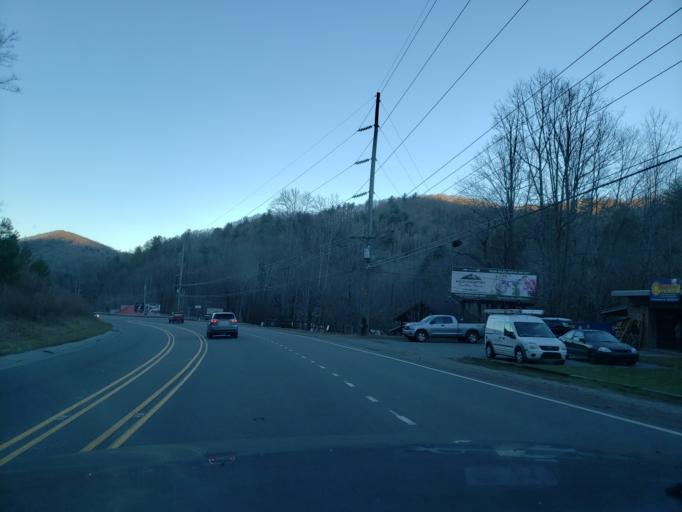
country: US
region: North Carolina
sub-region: Watauga County
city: Foscoe
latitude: 36.2042
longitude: -81.7344
